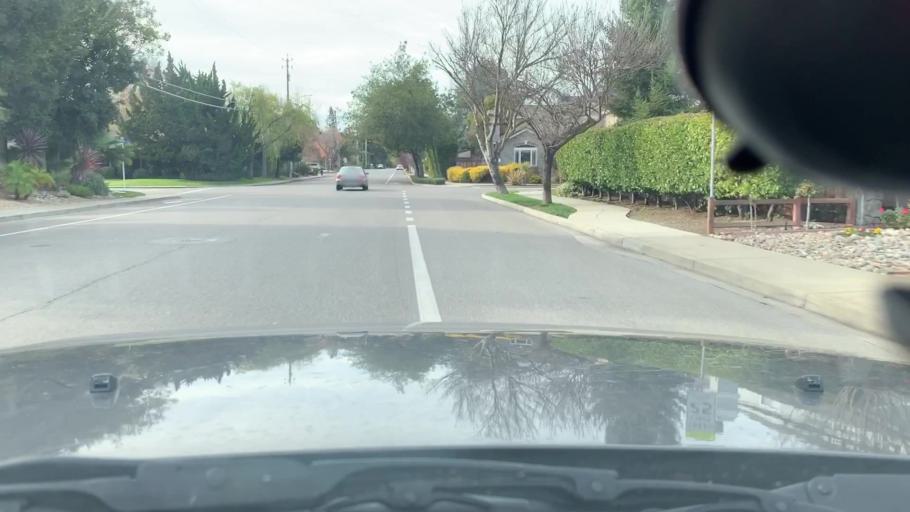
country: US
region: California
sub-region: Santa Clara County
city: Mountain View
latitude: 37.3613
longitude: -122.0704
